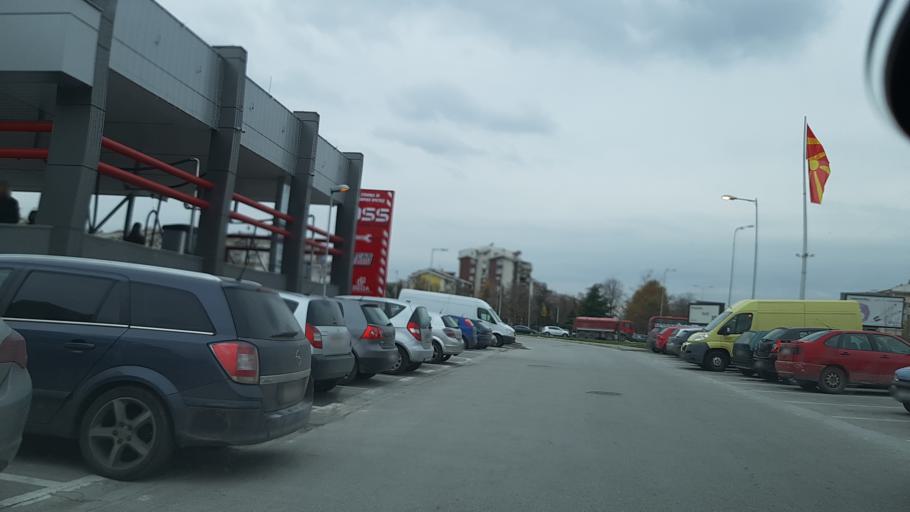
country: MK
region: Kisela Voda
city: Usje
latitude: 41.9818
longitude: 21.4722
